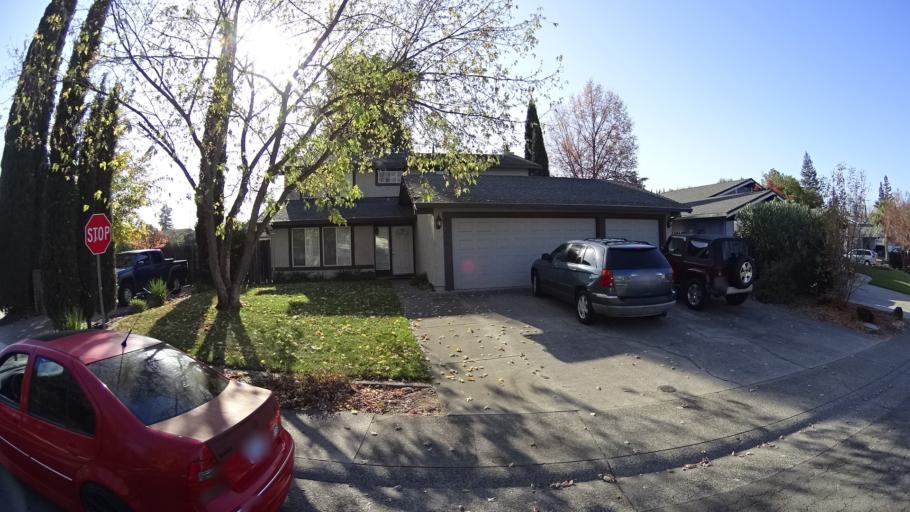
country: US
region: California
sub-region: Sacramento County
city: Citrus Heights
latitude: 38.6967
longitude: -121.2721
